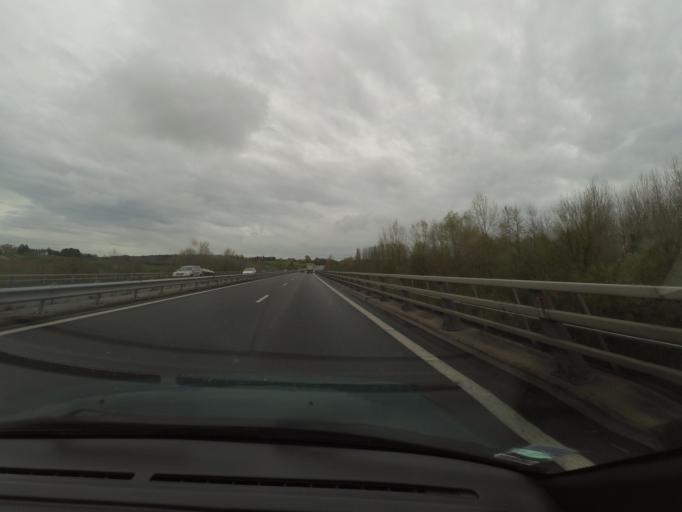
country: FR
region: Pays de la Loire
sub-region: Departement de Maine-et-Loire
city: Durtal
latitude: 47.6542
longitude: -0.2728
